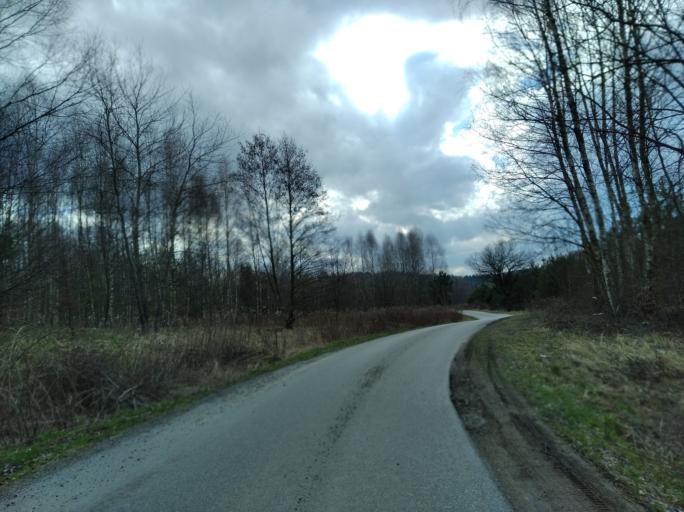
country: PL
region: Subcarpathian Voivodeship
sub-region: Powiat strzyzowski
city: Wysoka Strzyzowska
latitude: 49.7952
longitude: 21.7283
